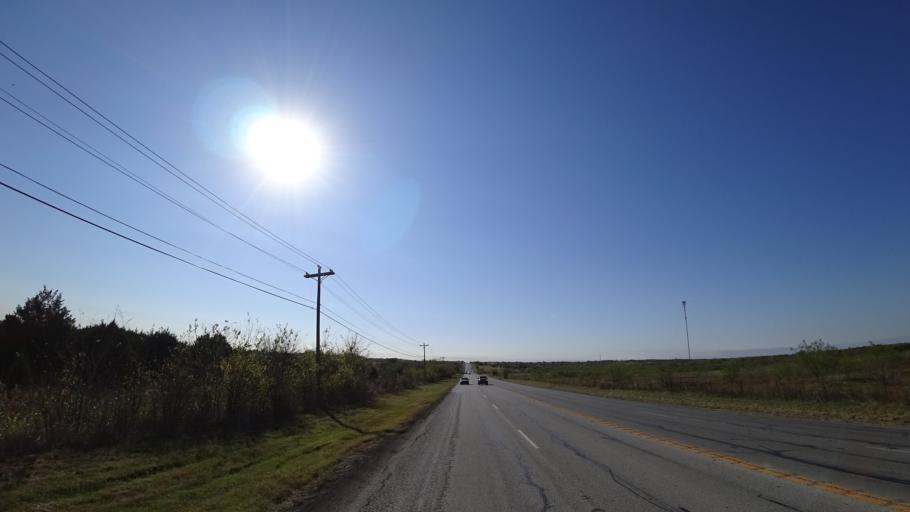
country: US
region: Texas
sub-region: Travis County
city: Onion Creek
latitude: 30.1347
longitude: -97.6963
